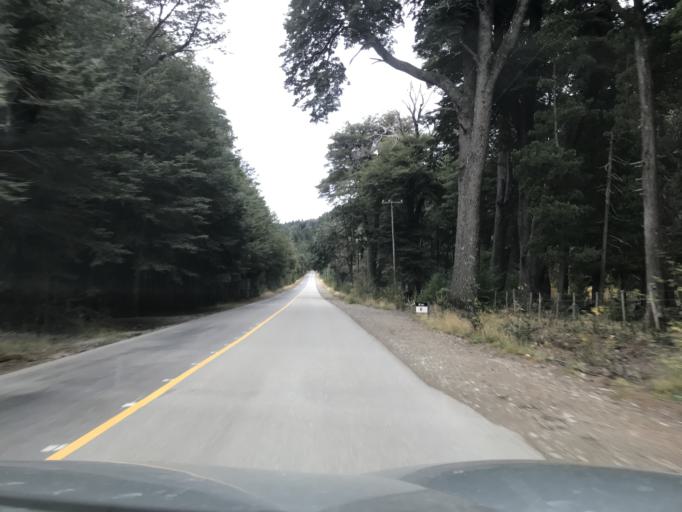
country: AR
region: Rio Negro
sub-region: Departamento de Bariloche
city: San Carlos de Bariloche
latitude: -41.0842
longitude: -71.5449
